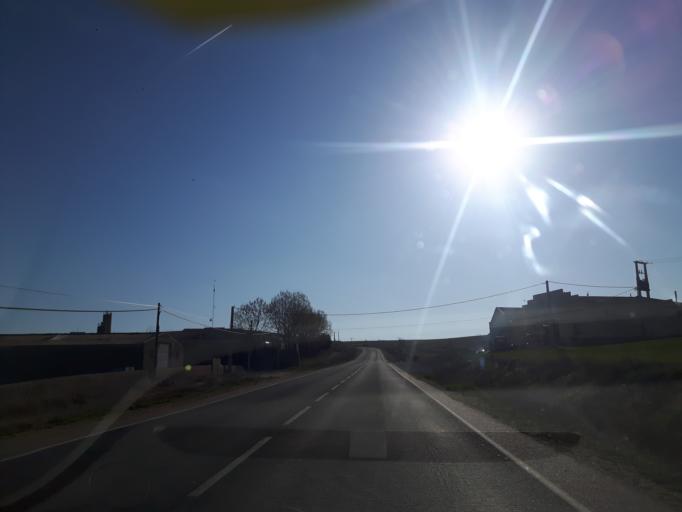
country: ES
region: Castille and Leon
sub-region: Provincia de Salamanca
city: Alba de Tormes
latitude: 40.8285
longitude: -5.4987
